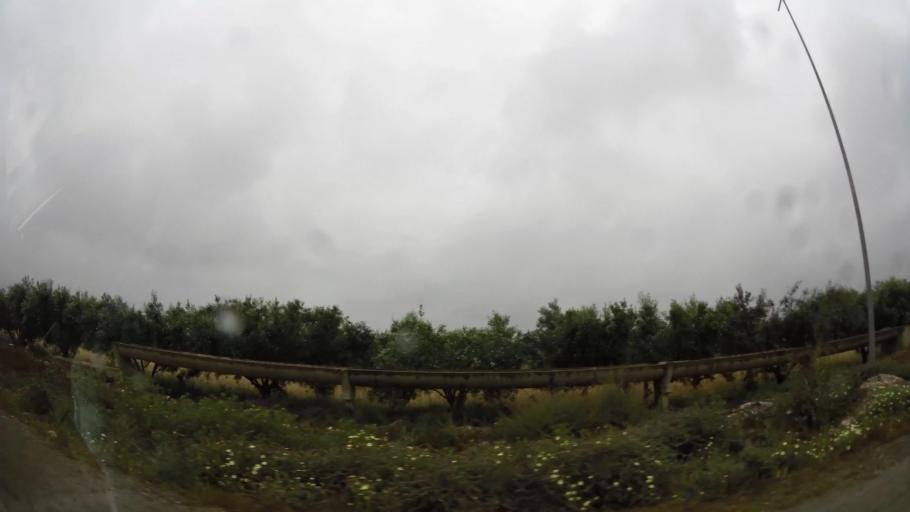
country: MA
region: Taza-Al Hoceima-Taounate
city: Imzourene
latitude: 35.1536
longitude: -3.8244
